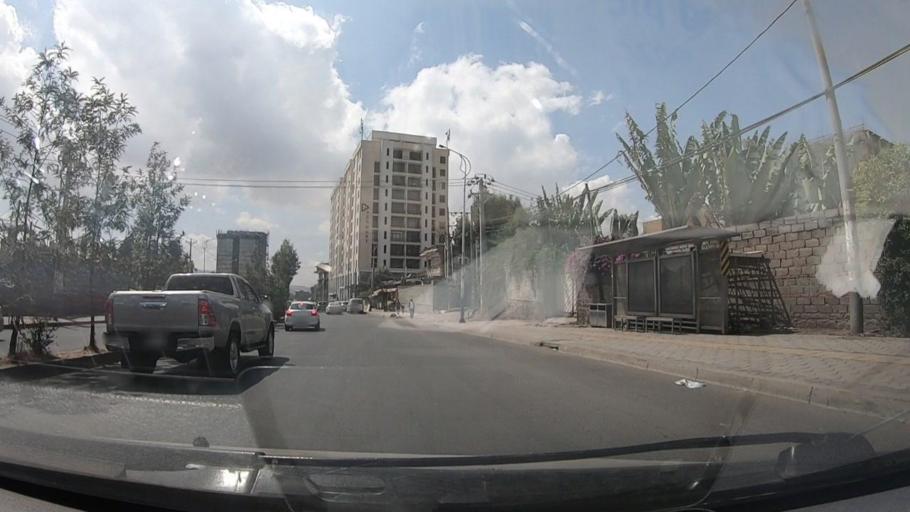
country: ET
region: Adis Abeba
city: Addis Ababa
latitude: 8.9880
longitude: 38.7223
